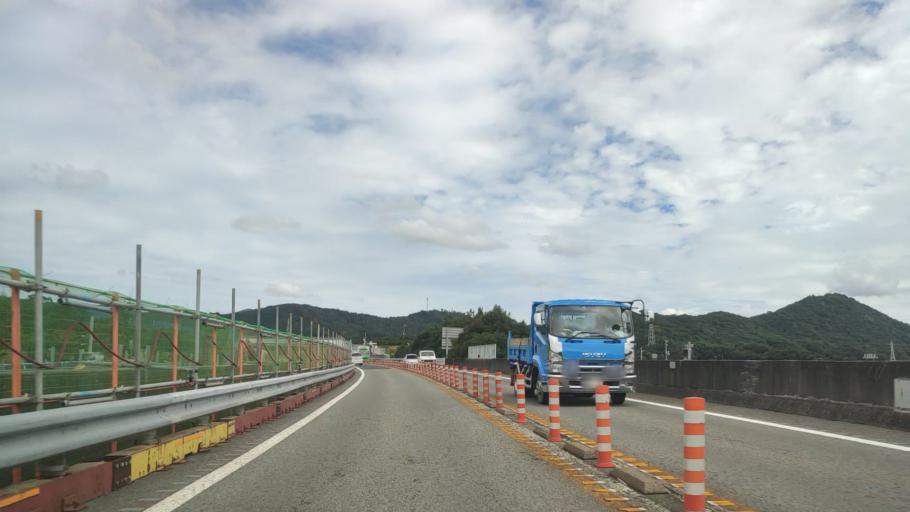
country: JP
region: Wakayama
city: Gobo
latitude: 33.9069
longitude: 135.1932
